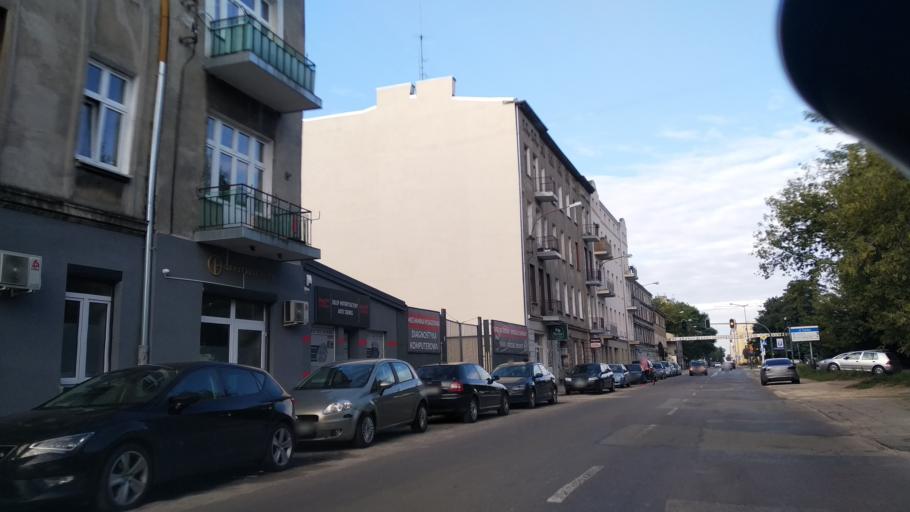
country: PL
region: Lodz Voivodeship
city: Lodz
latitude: 51.7671
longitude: 19.4750
